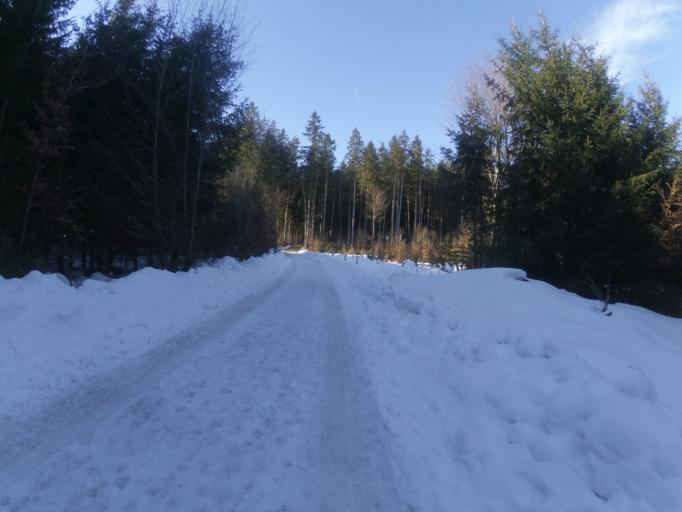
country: DE
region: Bavaria
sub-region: Upper Bavaria
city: Aying
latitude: 47.9878
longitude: 11.7498
